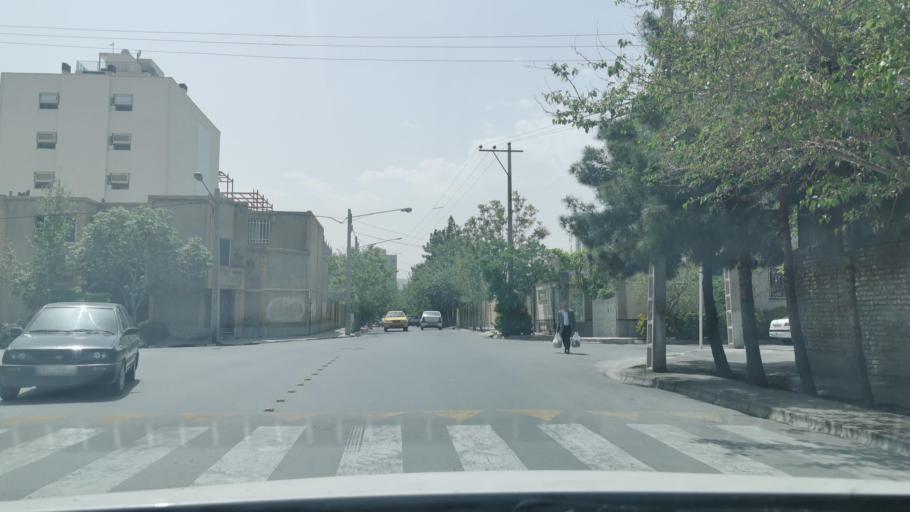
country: IR
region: Razavi Khorasan
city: Mashhad
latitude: 36.3357
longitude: 59.4813
